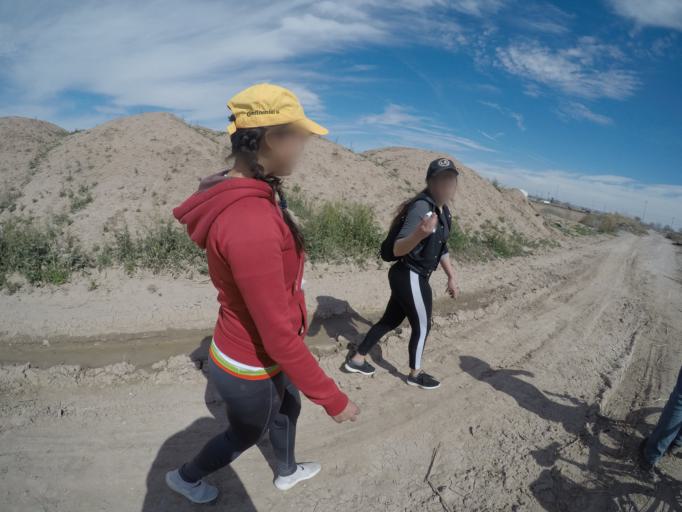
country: US
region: Texas
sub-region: El Paso County
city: Socorro
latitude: 31.6481
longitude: -106.3472
